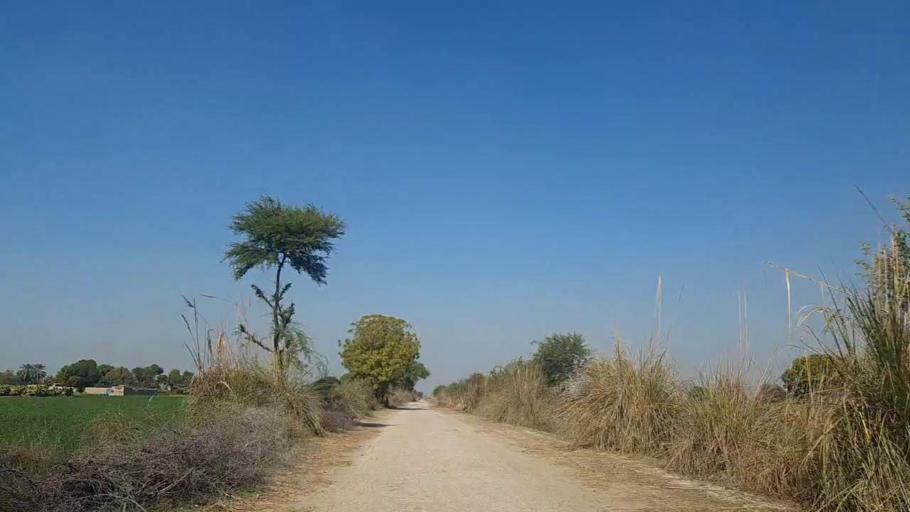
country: PK
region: Sindh
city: Sakrand
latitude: 26.2531
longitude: 68.2207
